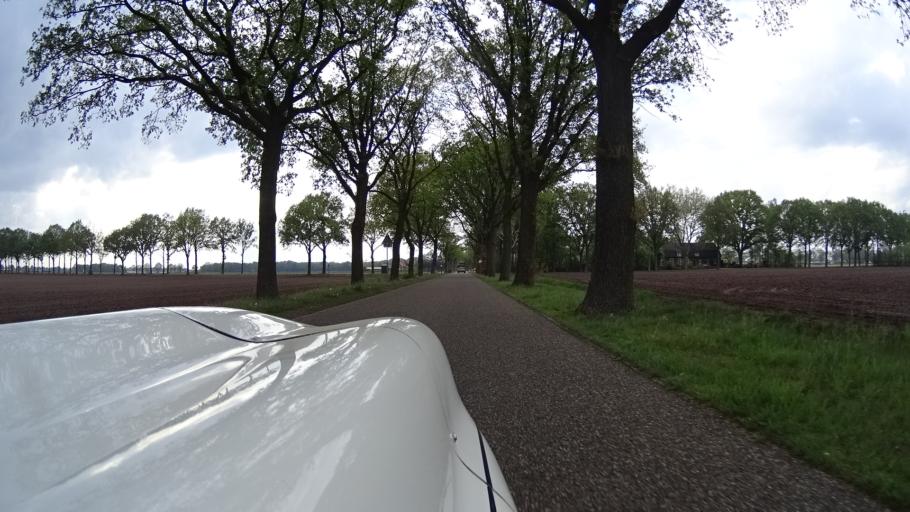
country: NL
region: North Brabant
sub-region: Gemeente Uden
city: Odiliapeel
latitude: 51.6109
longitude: 5.7316
